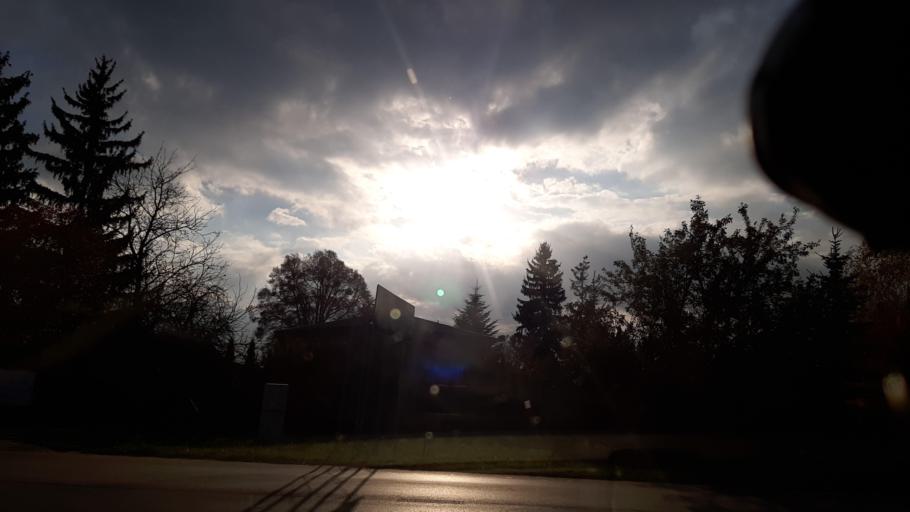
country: PL
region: Lublin Voivodeship
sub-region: Powiat pulawski
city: Naleczow
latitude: 51.3085
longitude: 22.2195
